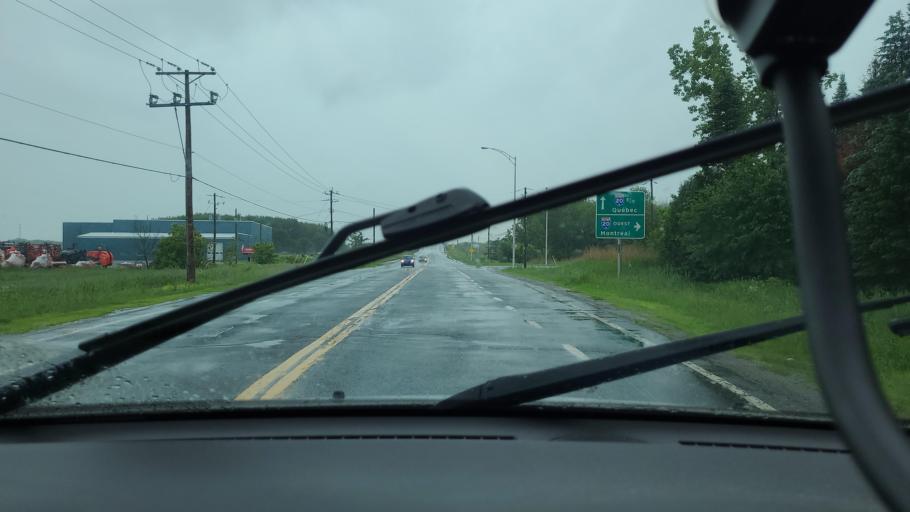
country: CA
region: Quebec
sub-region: Monteregie
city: Beloeil
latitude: 45.6109
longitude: -73.0996
